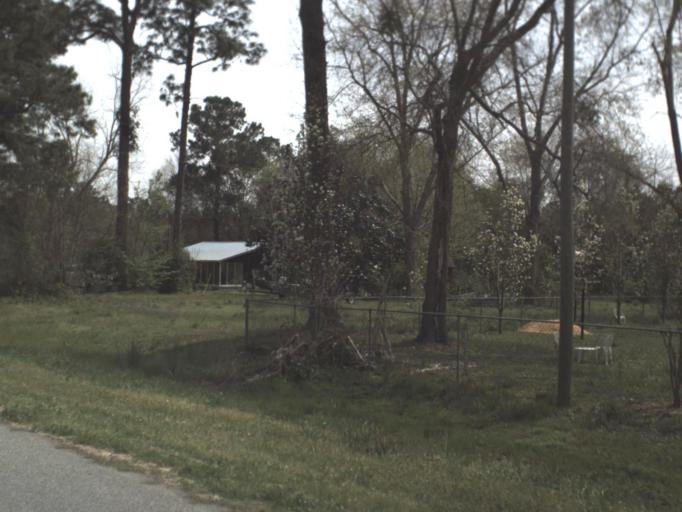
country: US
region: Alabama
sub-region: Geneva County
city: Geneva
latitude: 30.9411
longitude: -85.8165
